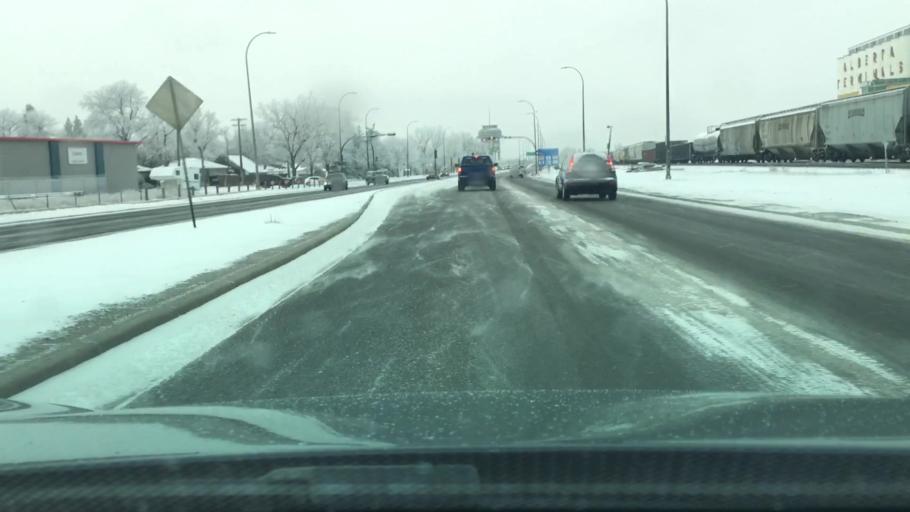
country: CA
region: Alberta
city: Lethbridge
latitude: 49.6981
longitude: -112.7999
